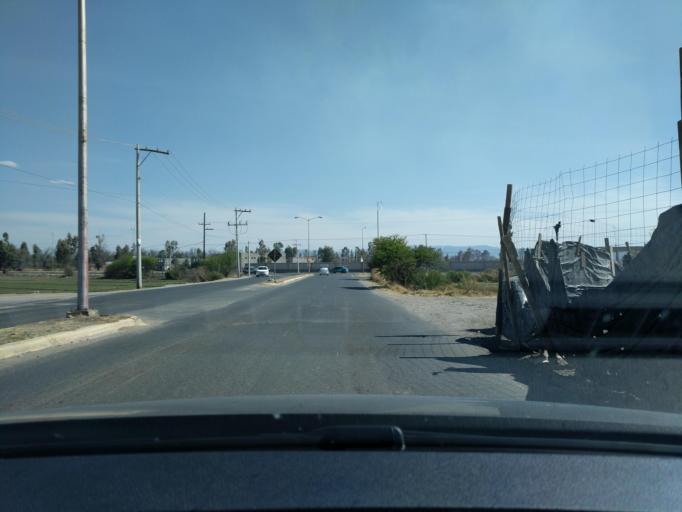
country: MX
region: Durango
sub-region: Durango
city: Sebastian Lerdo de Tejada
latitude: 23.9843
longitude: -104.6021
